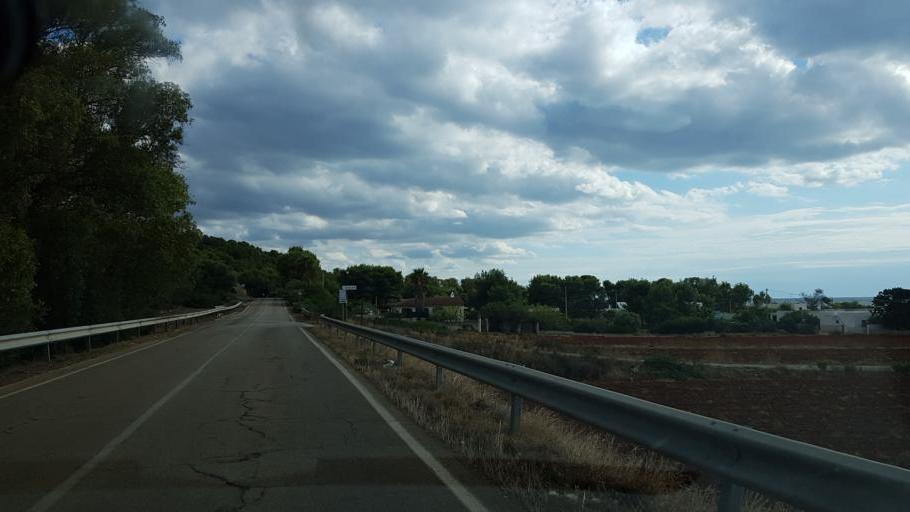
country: IT
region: Apulia
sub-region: Provincia di Lecce
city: Nardo
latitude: 40.1695
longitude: 17.9491
